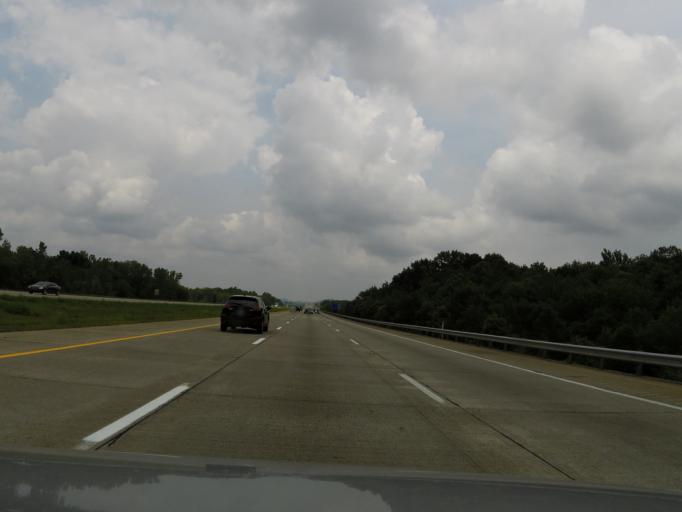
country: US
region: Kentucky
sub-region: Bullitt County
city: Lebanon Junction
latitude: 37.7927
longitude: -85.7552
